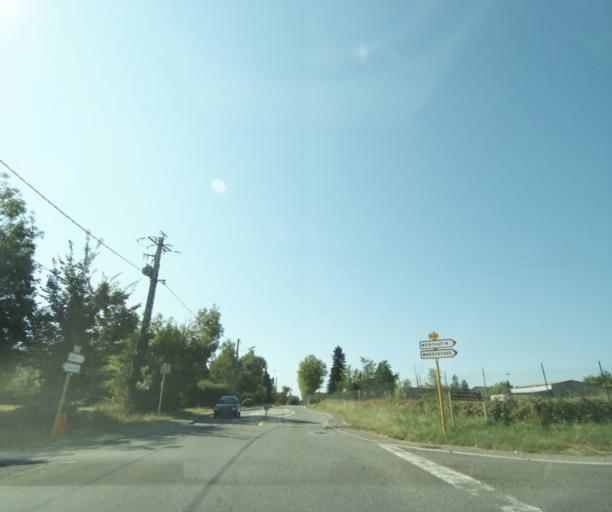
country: FR
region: Midi-Pyrenees
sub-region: Departement de la Haute-Garonne
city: Saint-Sulpice-sur-Leze
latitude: 43.3244
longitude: 1.3224
